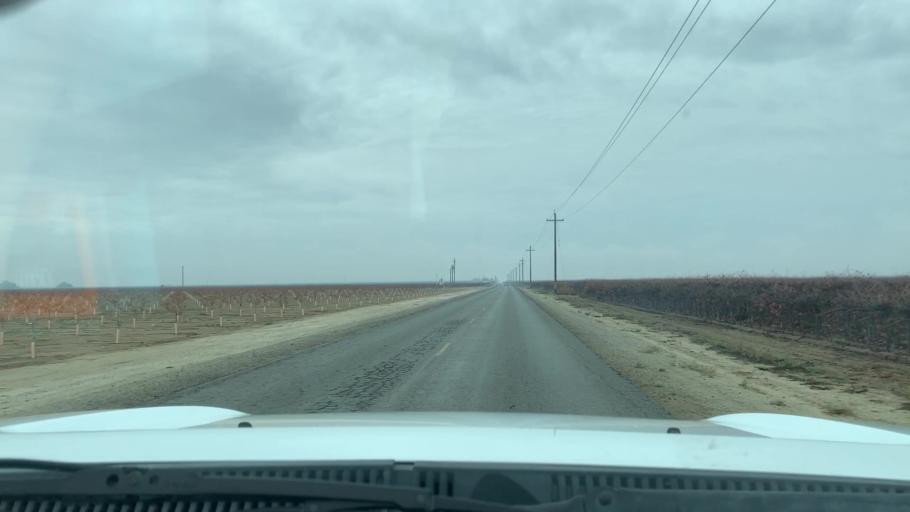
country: US
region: California
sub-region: Kern County
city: Delano
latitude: 35.7611
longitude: -119.3868
